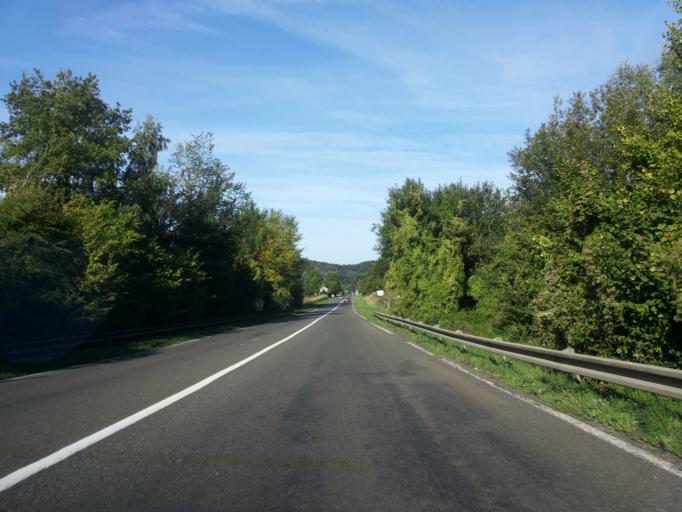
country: FR
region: Picardie
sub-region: Departement de l'Aisne
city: Crepy
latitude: 49.6113
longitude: 3.4850
